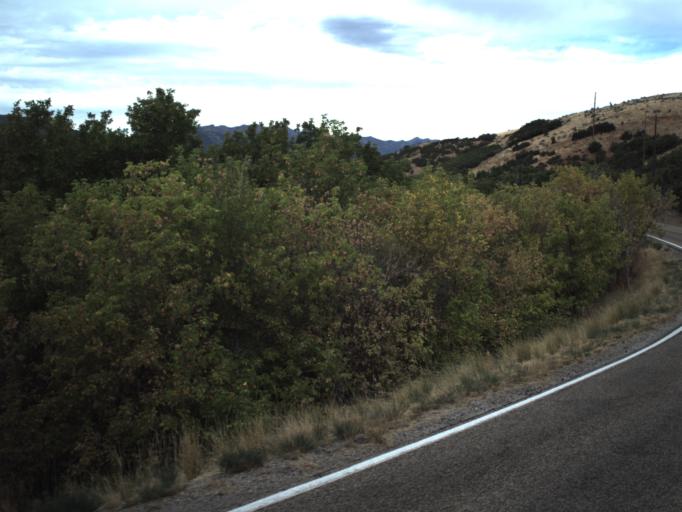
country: US
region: Utah
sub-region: Morgan County
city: Morgan
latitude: 40.9418
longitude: -111.6453
